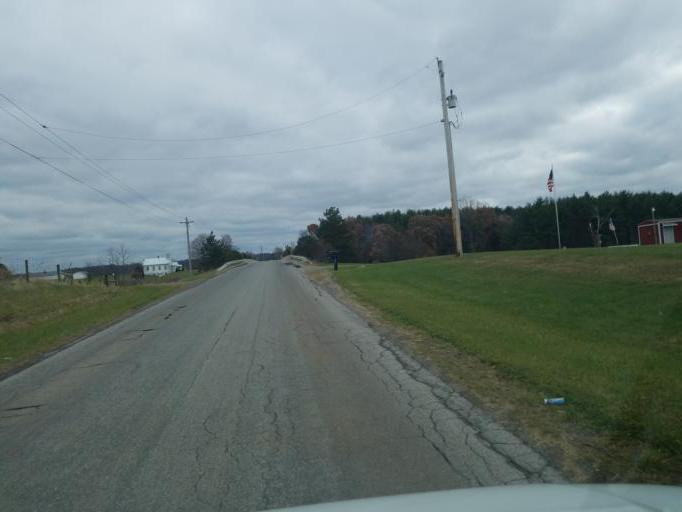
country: US
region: Ohio
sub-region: Richland County
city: Lexington
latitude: 40.5864
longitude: -82.5990
